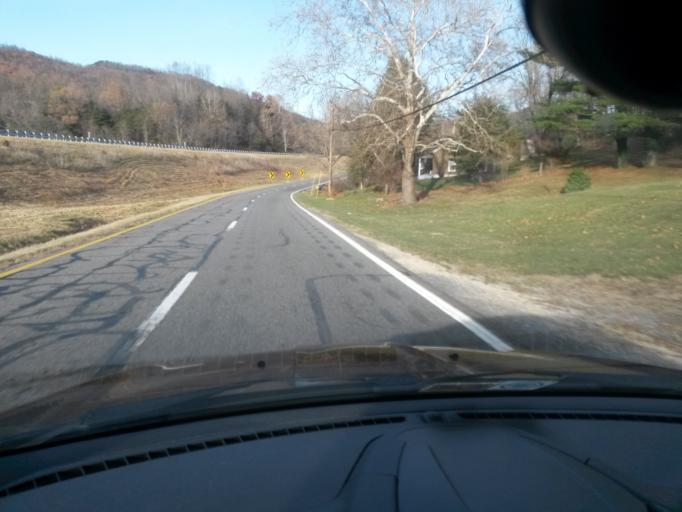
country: US
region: Virginia
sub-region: Botetourt County
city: Fincastle
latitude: 37.6242
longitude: -79.8200
